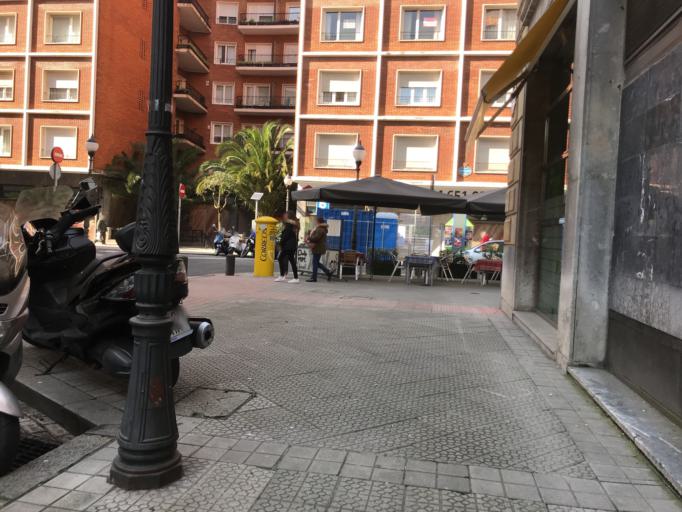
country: ES
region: Basque Country
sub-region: Bizkaia
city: Bilbao
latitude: 43.2666
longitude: -2.9347
